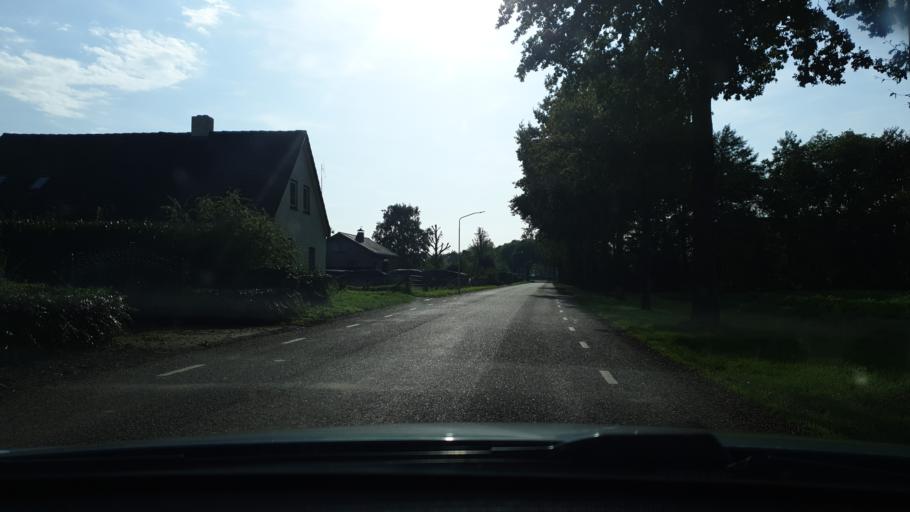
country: NL
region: Gelderland
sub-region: Gemeente Wijchen
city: Bergharen
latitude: 51.8745
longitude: 5.7001
